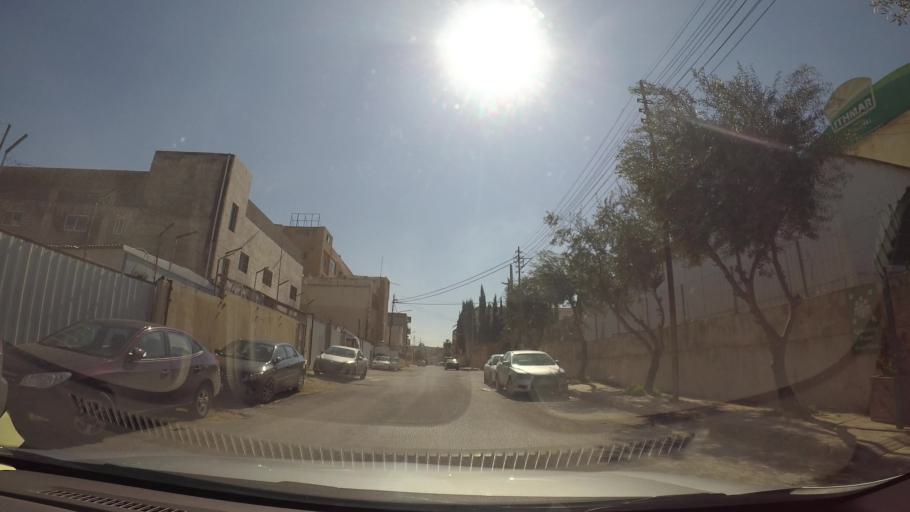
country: JO
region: Amman
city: Al Bunayyat ash Shamaliyah
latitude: 31.9098
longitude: 35.9115
